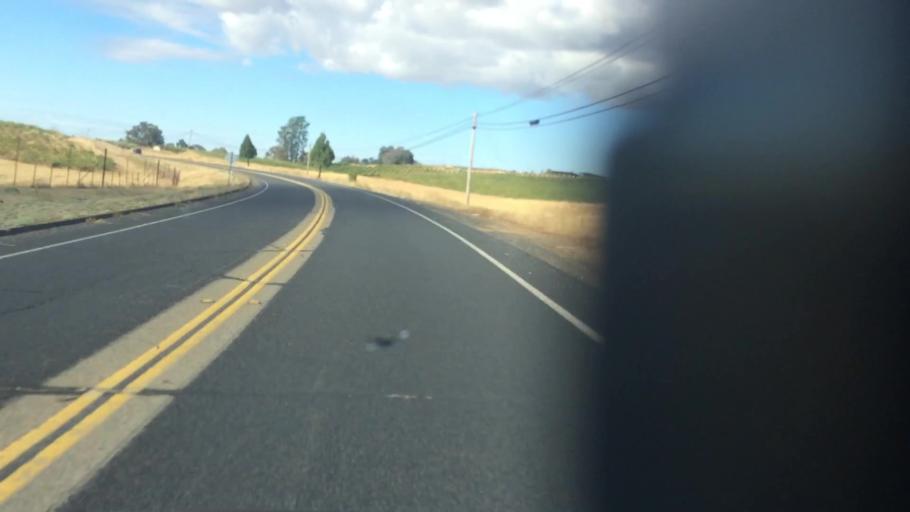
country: US
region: California
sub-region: Amador County
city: Plymouth
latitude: 38.5310
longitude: -120.8051
